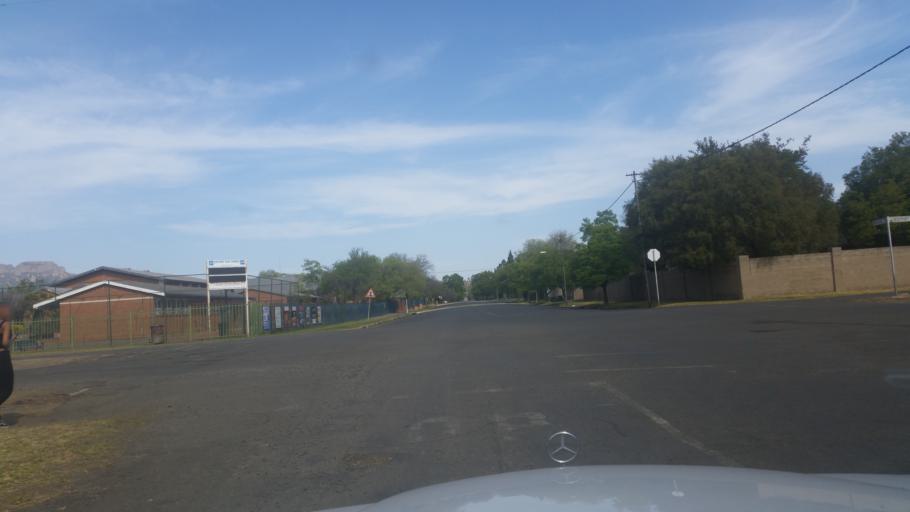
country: ZA
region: Orange Free State
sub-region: Thabo Mofutsanyana District Municipality
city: Harrismith
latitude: -28.2670
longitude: 29.1295
